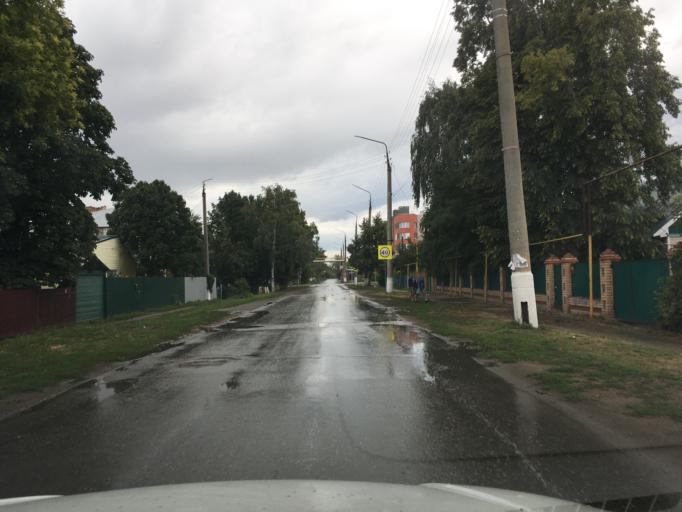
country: RU
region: Samara
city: Bezenchuk
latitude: 52.9823
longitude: 49.4392
